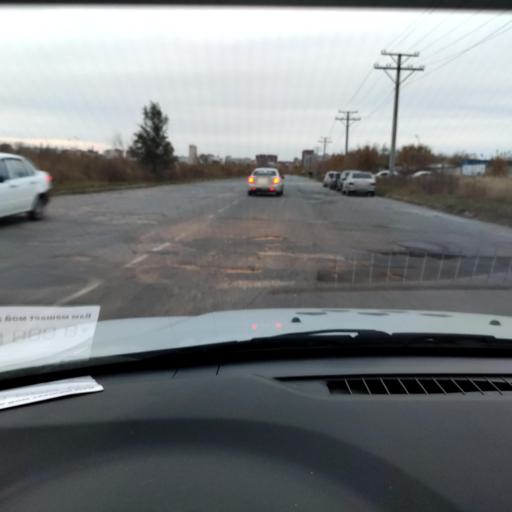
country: RU
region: Samara
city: Tol'yatti
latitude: 53.5572
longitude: 49.3292
